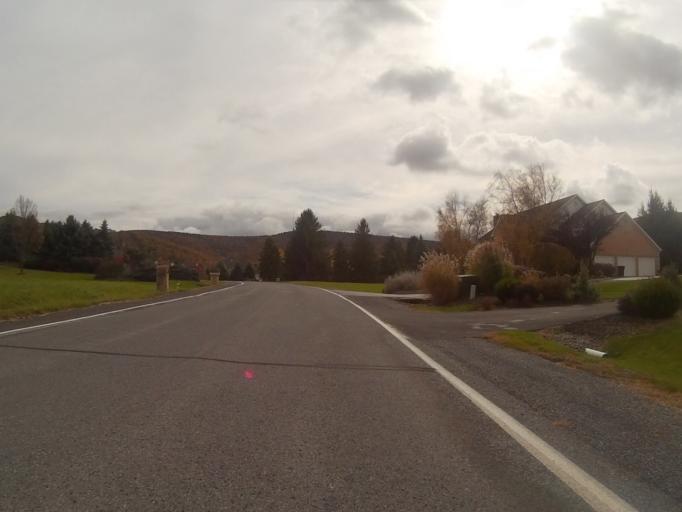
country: US
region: Pennsylvania
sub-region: Centre County
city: Boalsburg
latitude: 40.7768
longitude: -77.7608
